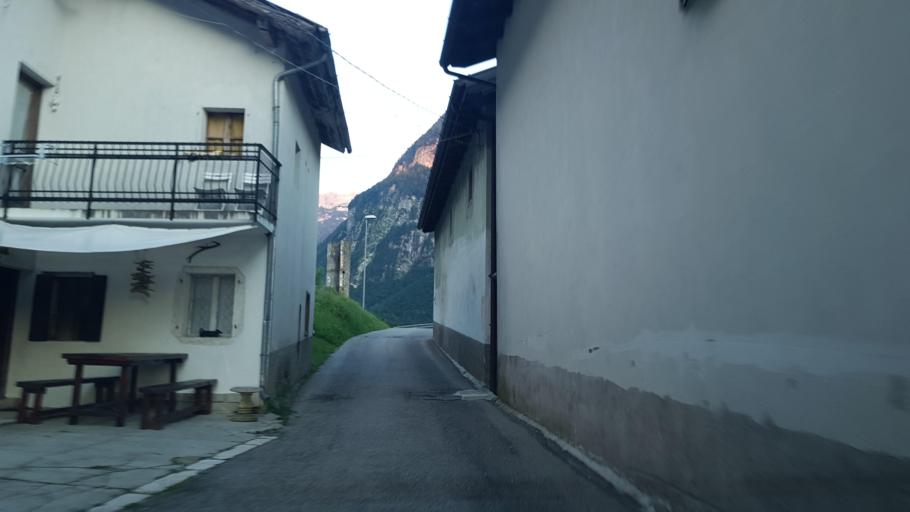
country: IT
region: Friuli Venezia Giulia
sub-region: Provincia di Udine
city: Malborghetto
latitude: 46.4012
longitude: 13.4247
